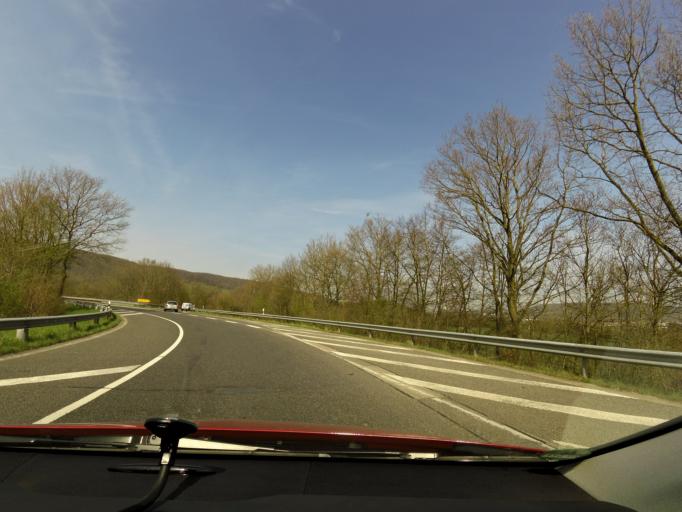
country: DE
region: Rheinland-Pfalz
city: Sinzig
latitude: 50.5567
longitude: 7.2496
